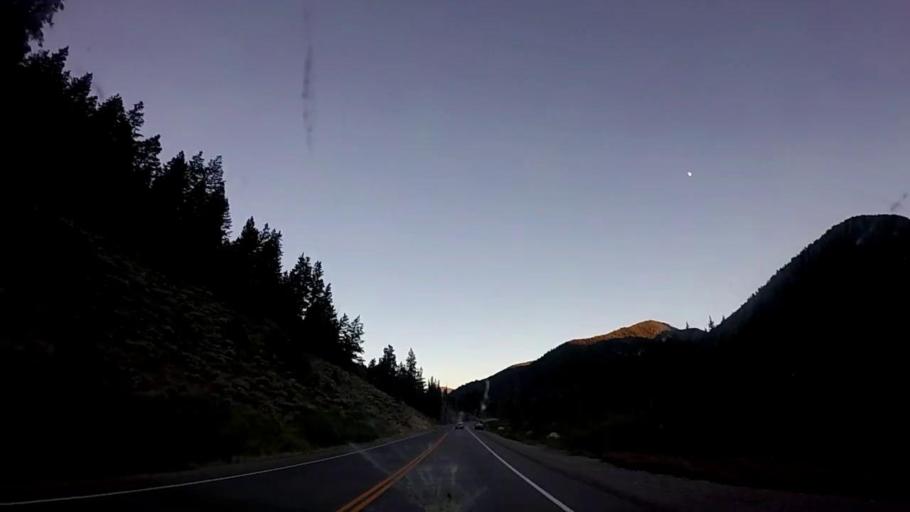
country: US
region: Utah
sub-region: Summit County
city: Summit Park
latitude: 40.6477
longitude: -111.6454
